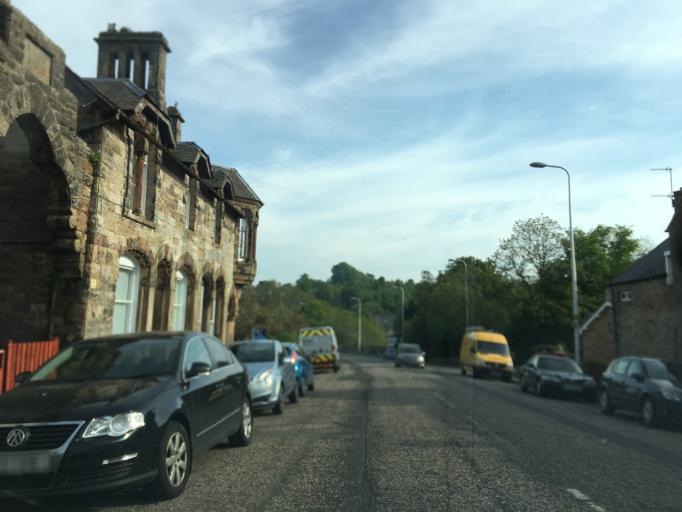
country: GB
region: Scotland
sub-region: Midlothian
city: Penicuik
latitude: 55.8248
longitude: -3.2219
